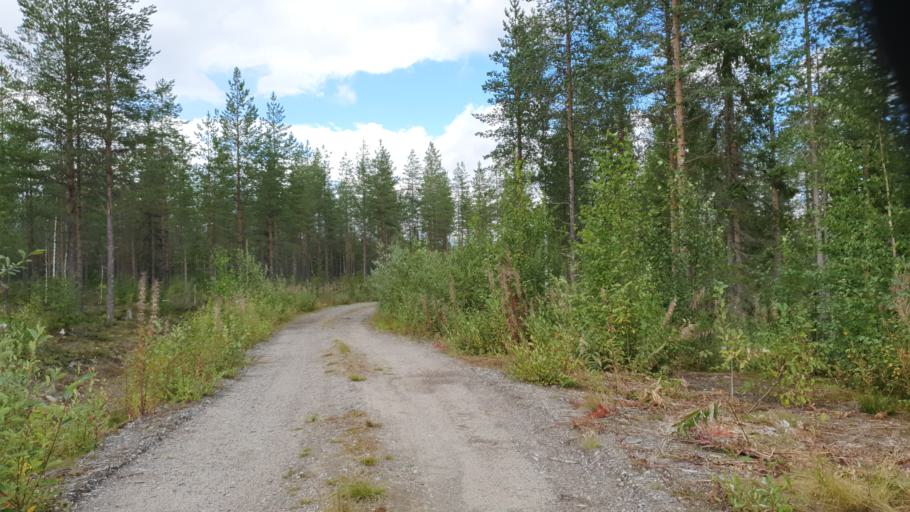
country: FI
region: Kainuu
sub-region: Kehys-Kainuu
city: Kuhmo
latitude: 64.1443
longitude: 29.3858
